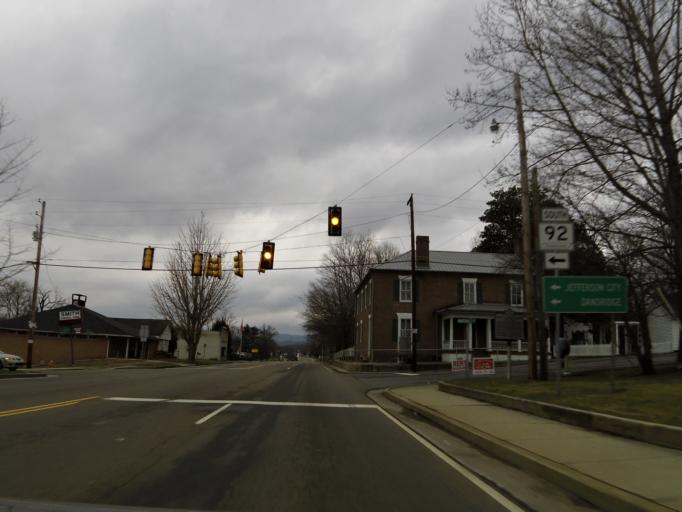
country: US
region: Tennessee
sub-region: Grainger County
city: Rutledge
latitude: 36.2808
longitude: -83.5145
